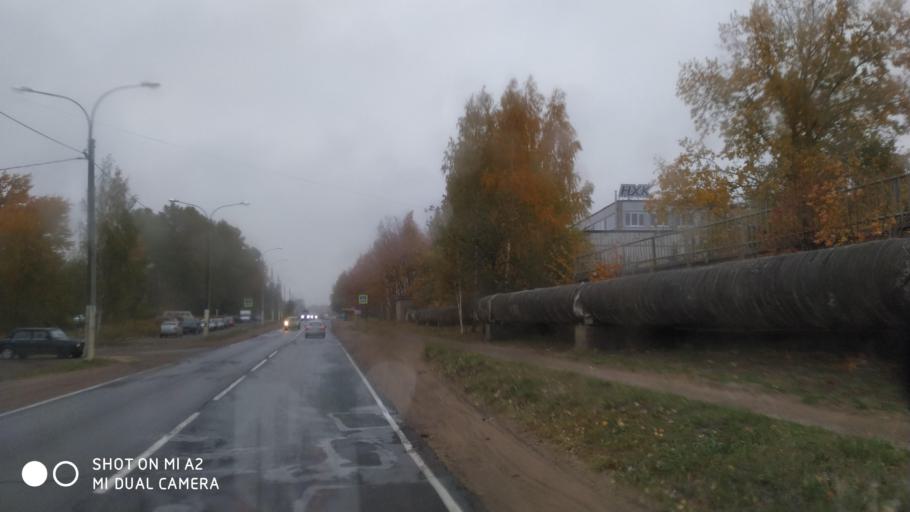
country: RU
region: Leningrad
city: Sosnovyy Bor
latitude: 59.8863
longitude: 29.1000
